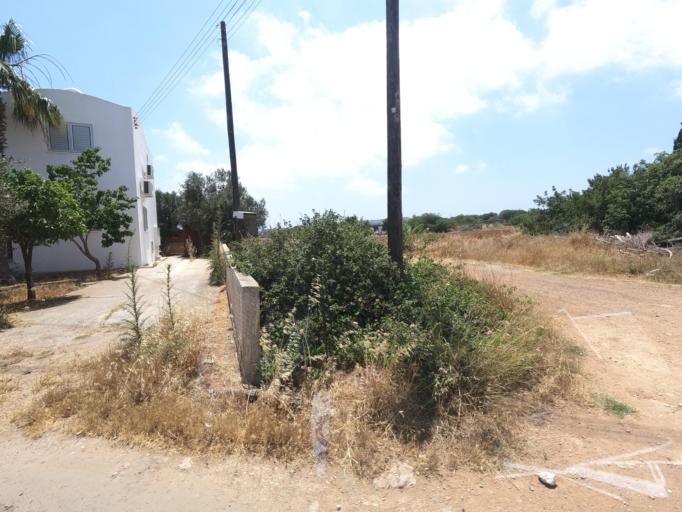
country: CY
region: Ammochostos
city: Protaras
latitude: 35.0323
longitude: 34.0274
